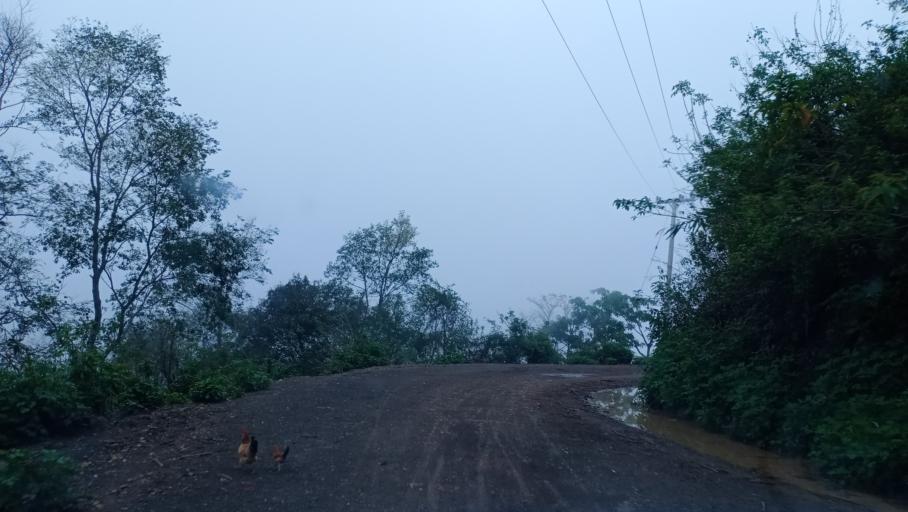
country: LA
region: Phongsali
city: Phongsali
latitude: 21.4884
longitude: 102.1626
